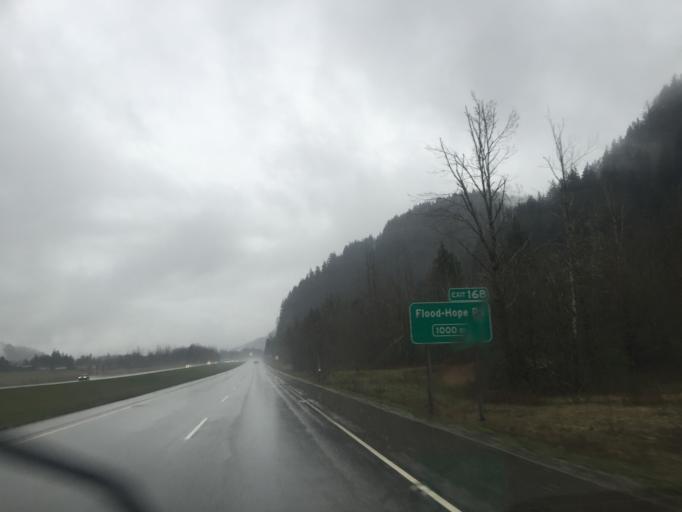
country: CA
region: British Columbia
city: Hope
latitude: 49.3622
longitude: -121.5045
